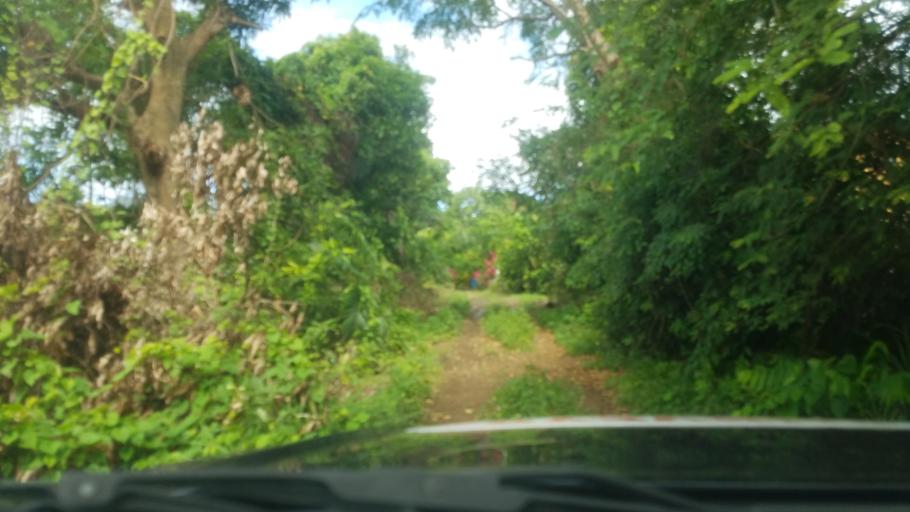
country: LC
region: Dennery Quarter
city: Dennery
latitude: 13.9323
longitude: -60.9227
